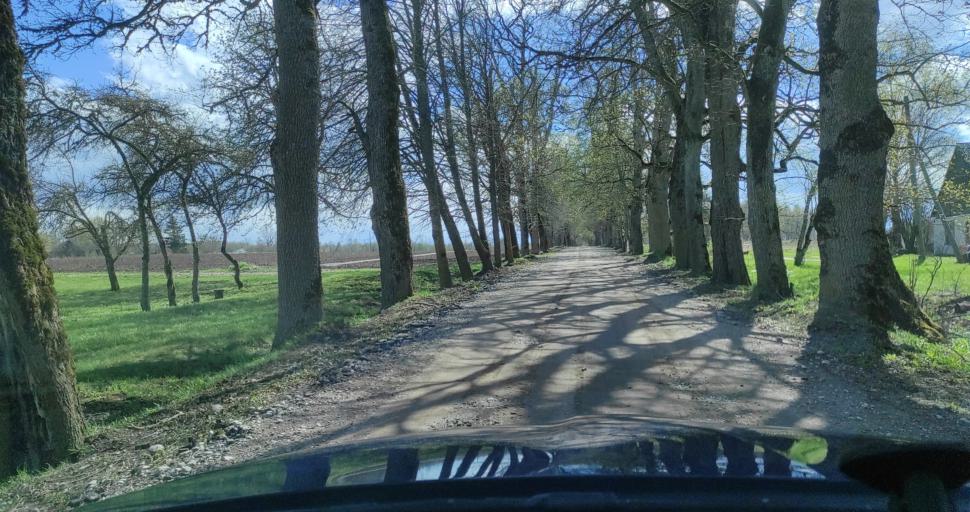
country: LV
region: Kuldigas Rajons
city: Kuldiga
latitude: 56.8625
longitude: 21.8134
